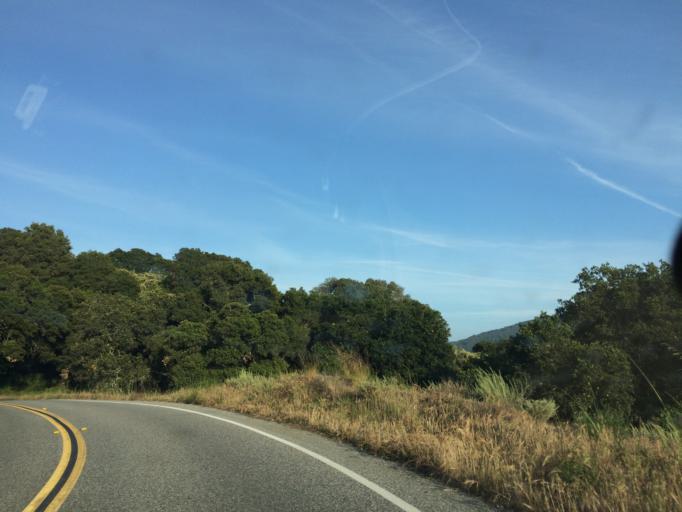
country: US
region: California
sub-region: Santa Clara County
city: Los Altos Hills
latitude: 37.3562
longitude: -122.1731
